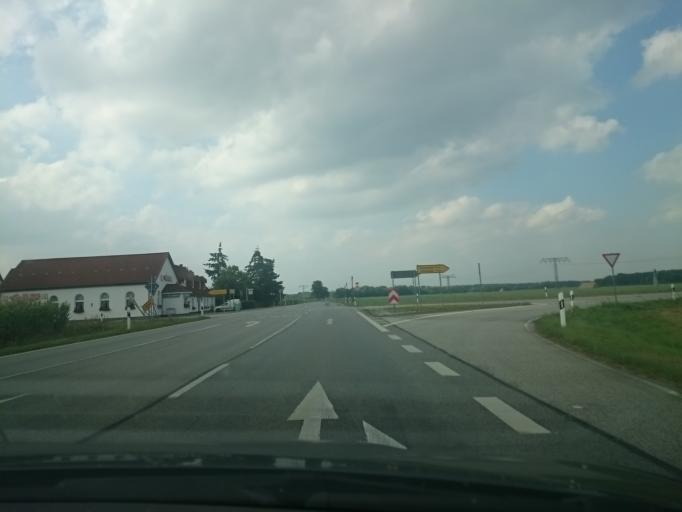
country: DE
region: Mecklenburg-Vorpommern
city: Ferdinandshof
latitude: 53.7085
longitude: 13.8478
